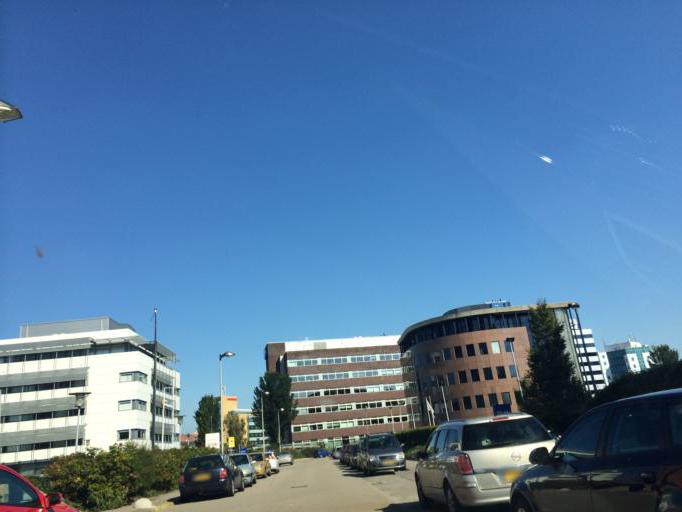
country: NL
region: South Holland
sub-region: Gemeente Rotterdam
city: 's-Gravenland
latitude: 51.9139
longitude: 4.5397
